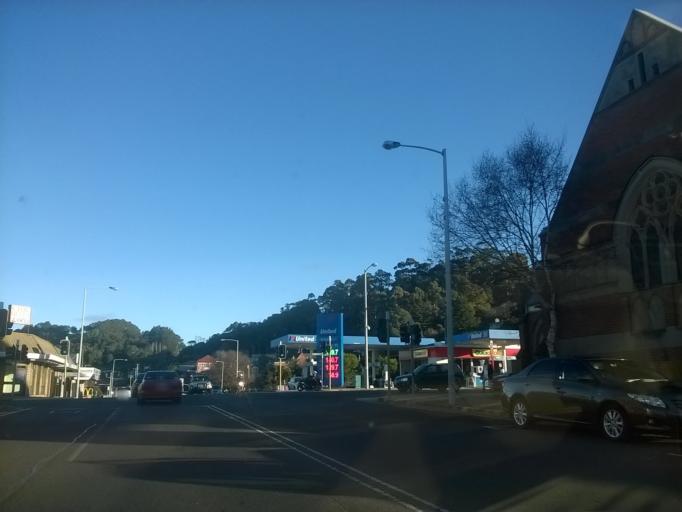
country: AU
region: Tasmania
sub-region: Burnie
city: Burnie
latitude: -41.0536
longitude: 145.9047
